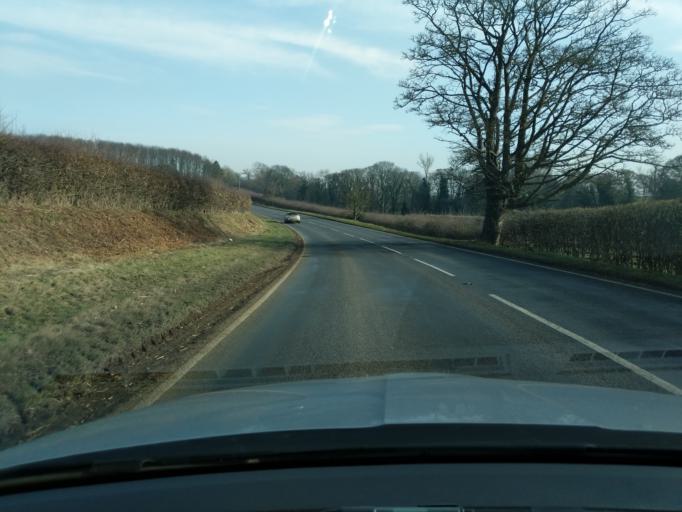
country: GB
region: England
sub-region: North Yorkshire
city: Bedale
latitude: 54.3085
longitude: -1.6460
